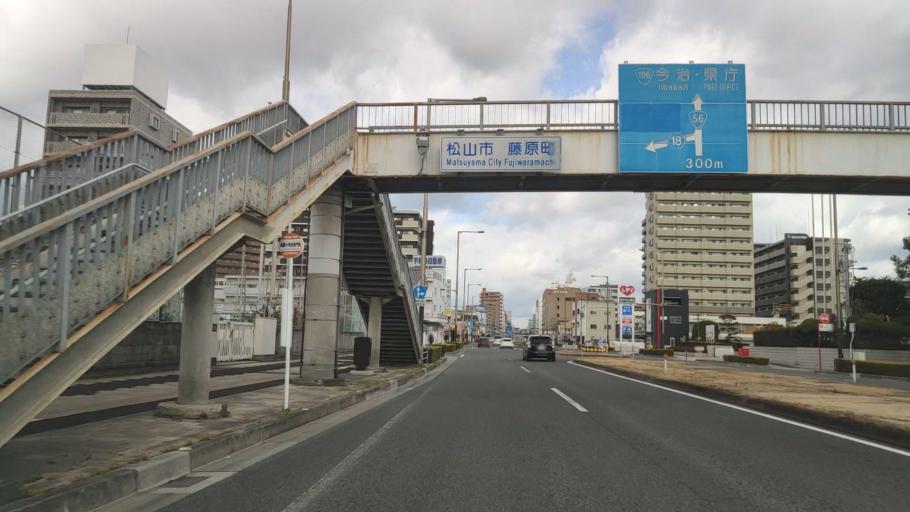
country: JP
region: Ehime
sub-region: Shikoku-chuo Shi
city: Matsuyama
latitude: 33.8318
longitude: 132.7588
